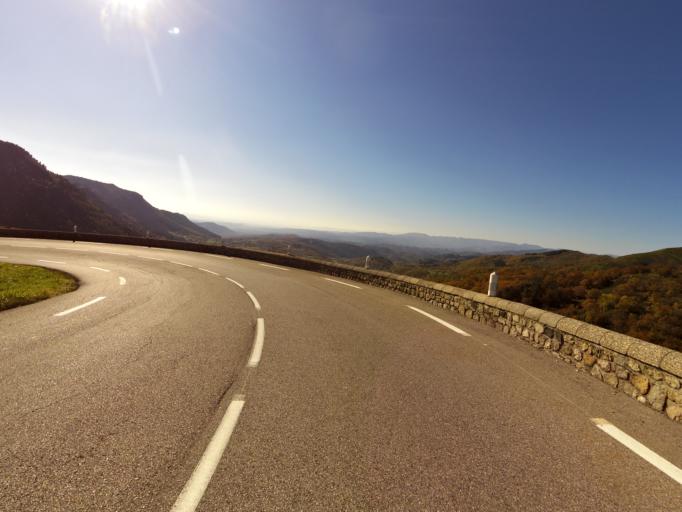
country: FR
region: Rhone-Alpes
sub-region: Departement de l'Ardeche
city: Saint-Priest
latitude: 44.7155
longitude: 4.4869
